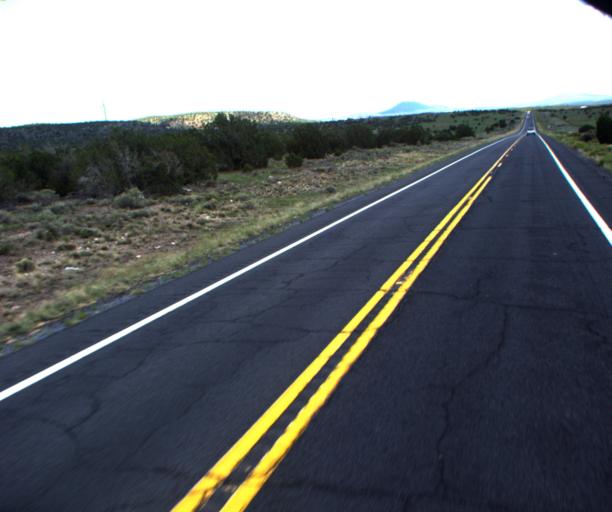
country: US
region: Arizona
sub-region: Coconino County
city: Williams
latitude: 35.5002
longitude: -112.1740
